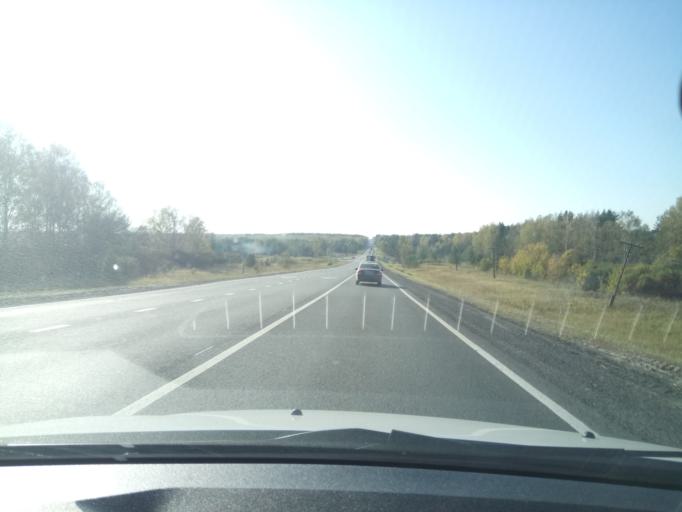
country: RU
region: Nizjnij Novgorod
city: Dal'neye Konstantinovo
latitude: 55.9627
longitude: 43.9745
